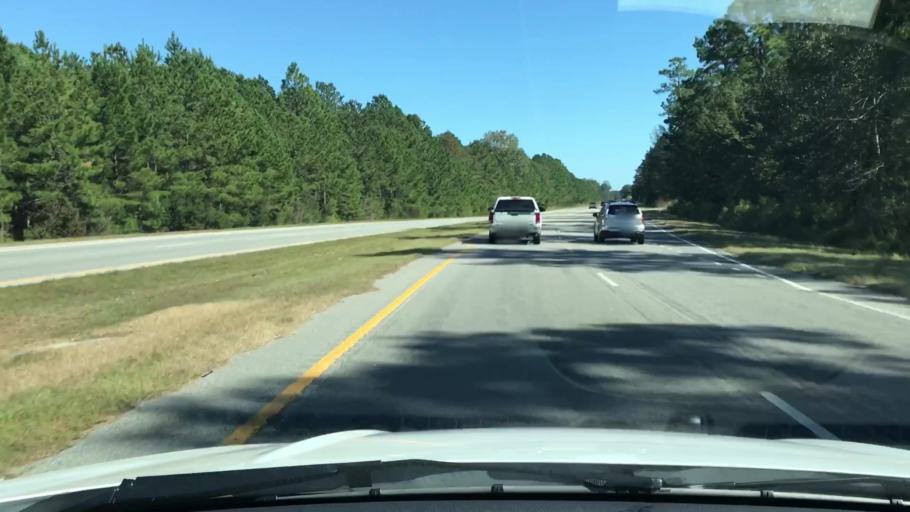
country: US
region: South Carolina
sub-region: Beaufort County
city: Bluffton
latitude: 32.3543
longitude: -80.9095
